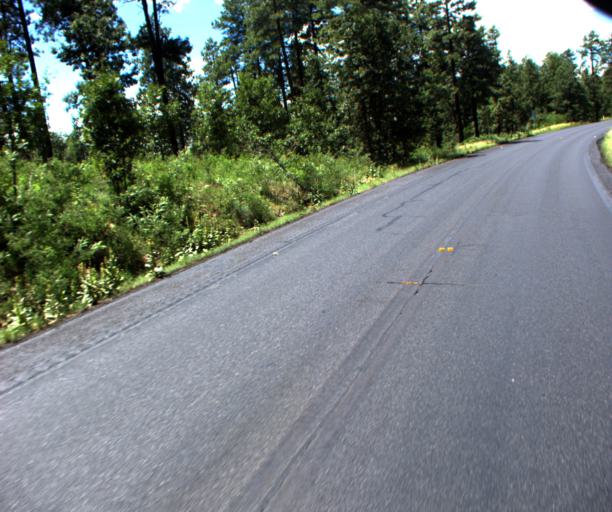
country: US
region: Arizona
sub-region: Gila County
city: Pine
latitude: 34.4661
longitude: -111.4463
